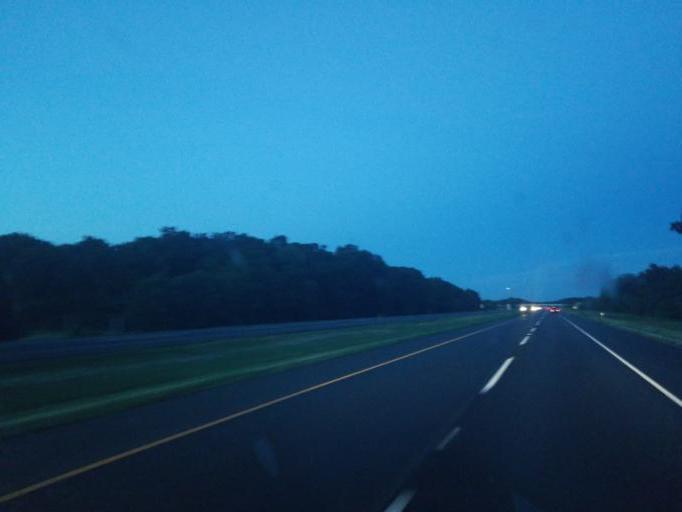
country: US
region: Indiana
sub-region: Saint Joseph County
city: Granger
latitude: 41.7311
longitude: -86.0730
